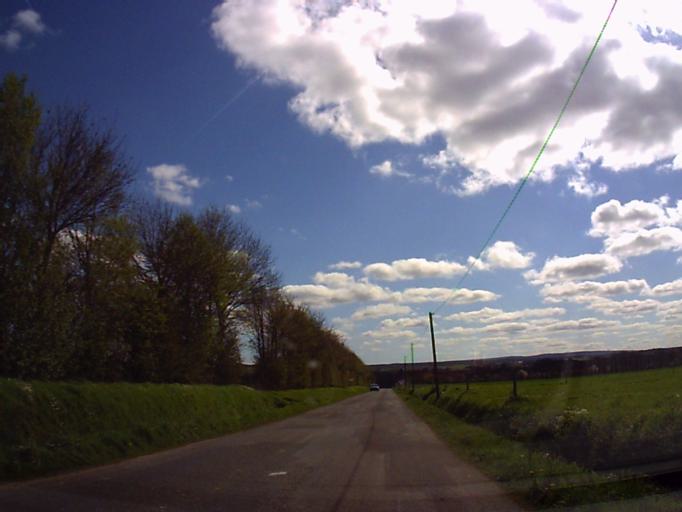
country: FR
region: Brittany
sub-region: Departement d'Ille-et-Vilaine
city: Saint-Meen-le-Grand
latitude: 48.1385
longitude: -2.1574
